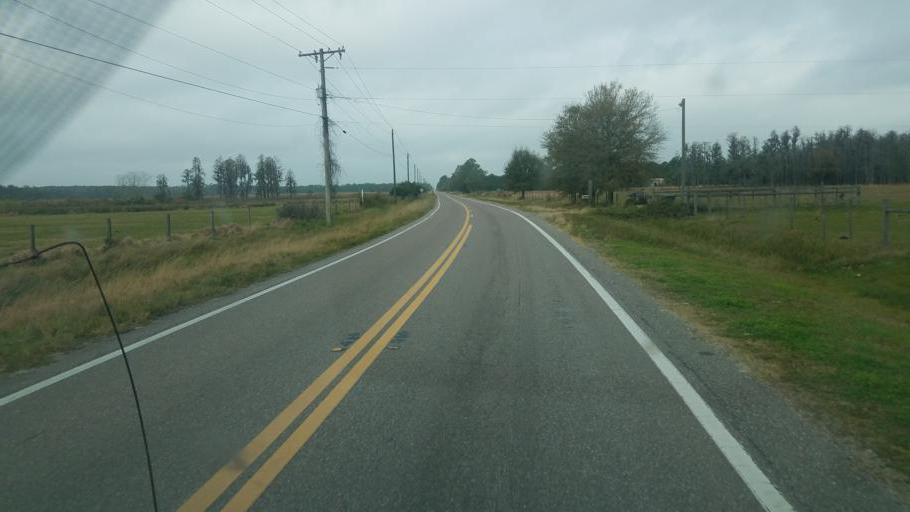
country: US
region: Florida
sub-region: Polk County
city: Polk City
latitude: 28.2591
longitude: -81.8569
